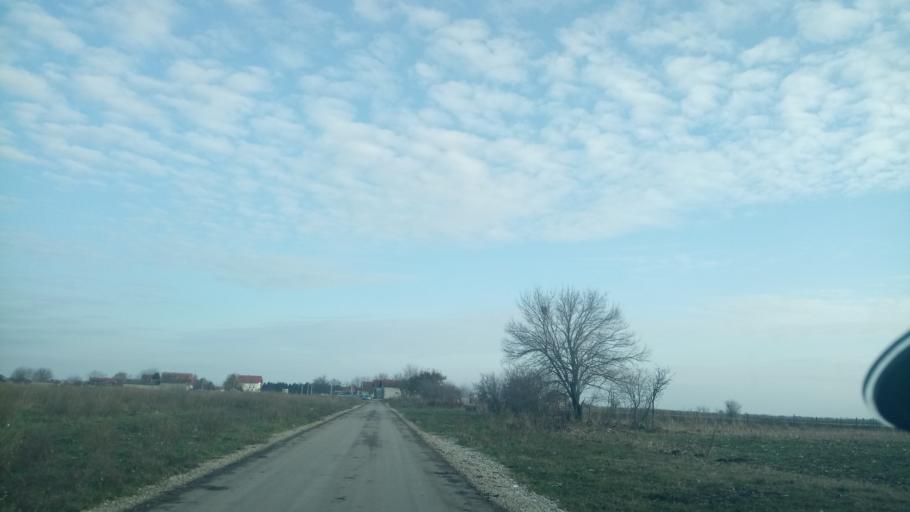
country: RS
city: Vojka
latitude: 44.9333
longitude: 20.1349
